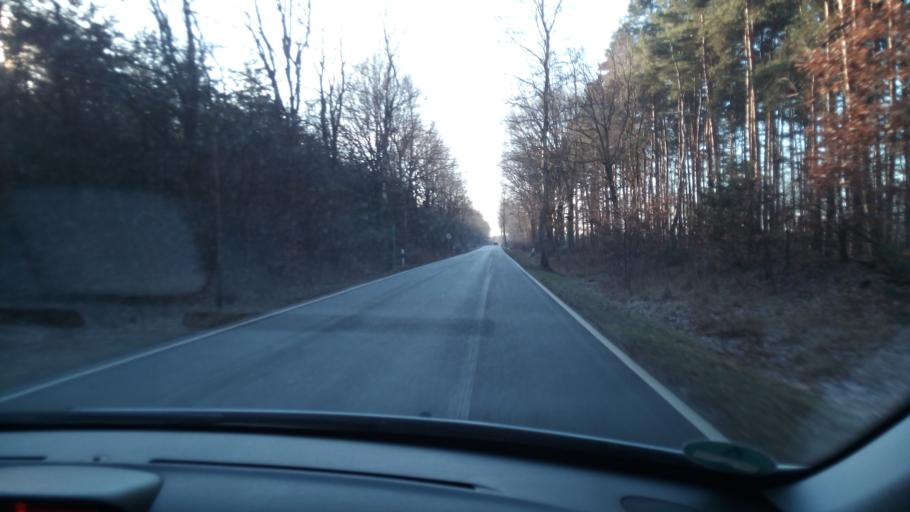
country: DE
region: Schleswig-Holstein
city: Brothen
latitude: 53.4956
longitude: 10.6736
